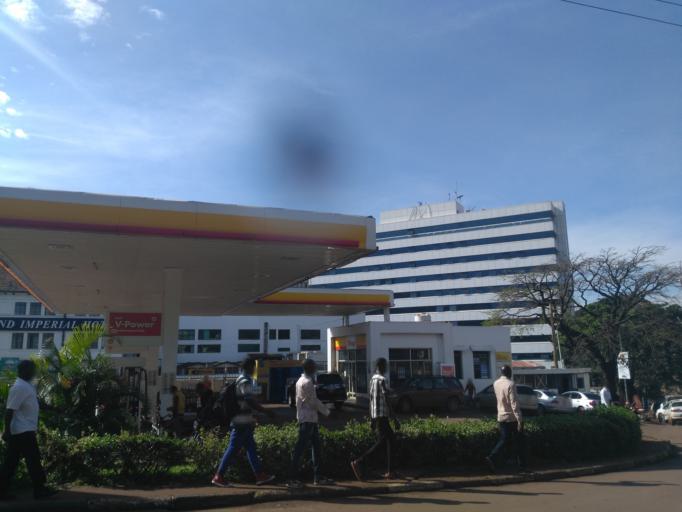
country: UG
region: Central Region
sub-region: Kampala District
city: Kampala
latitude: 0.3158
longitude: 32.5804
